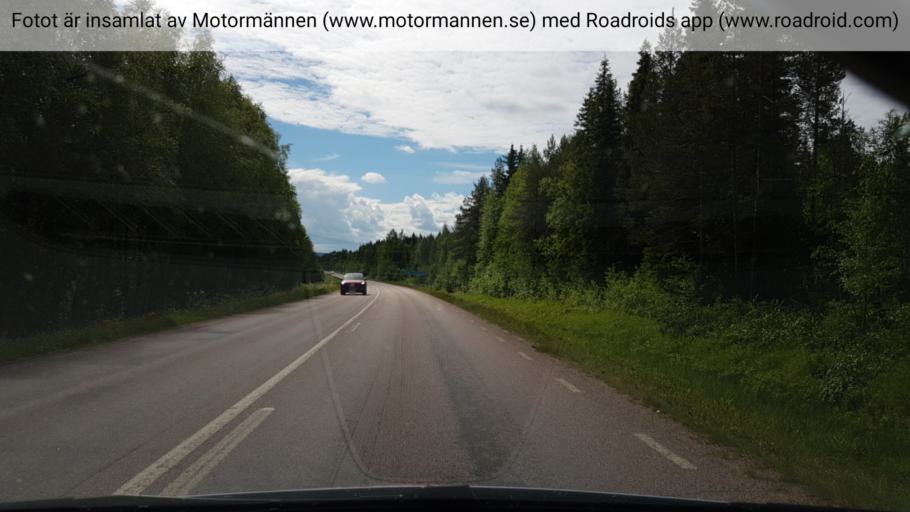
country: SE
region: Norrbotten
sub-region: Overtornea Kommun
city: OEvertornea
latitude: 66.4459
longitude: 23.6168
